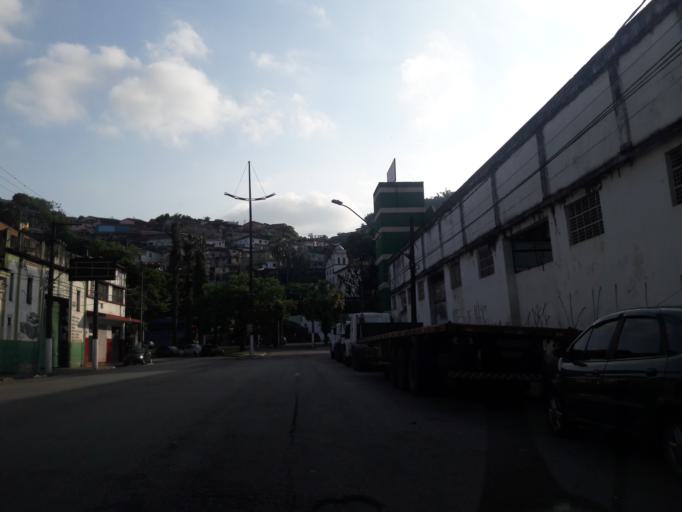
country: BR
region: Sao Paulo
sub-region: Santos
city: Santos
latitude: -23.9335
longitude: -46.3349
